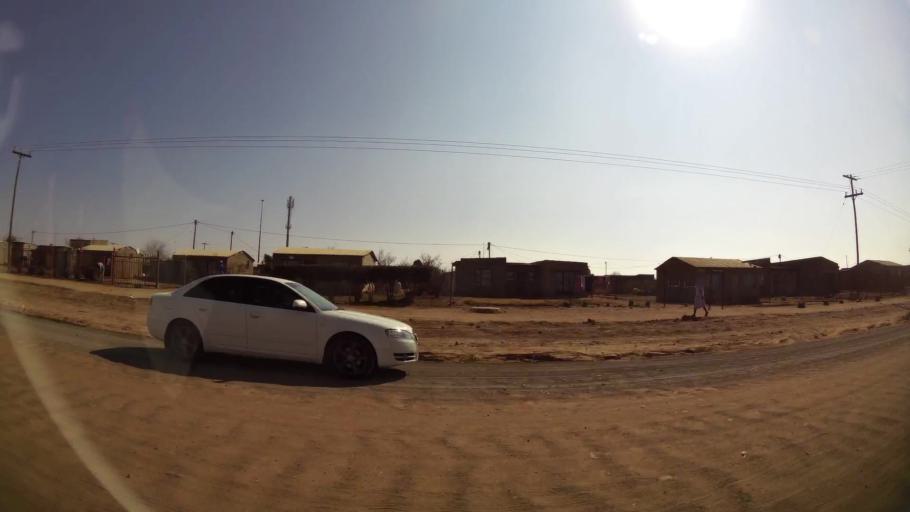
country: ZA
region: Orange Free State
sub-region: Mangaung Metropolitan Municipality
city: Bloemfontein
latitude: -29.1935
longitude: 26.2803
